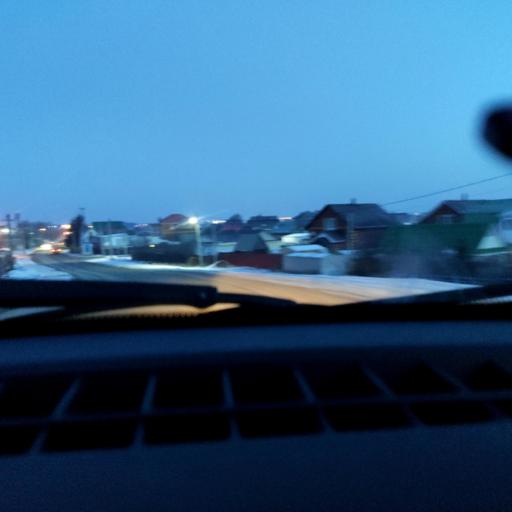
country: RU
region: Bashkortostan
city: Ufa
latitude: 54.6067
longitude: 55.9434
